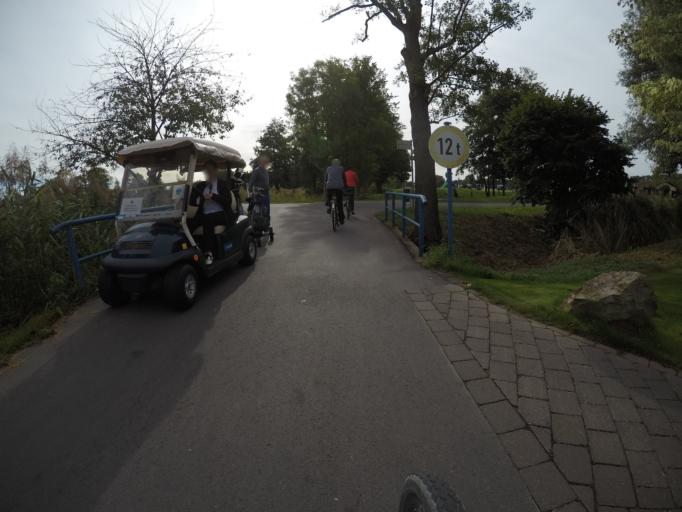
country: DE
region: Baden-Wuerttemberg
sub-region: Karlsruhe Region
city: Kronau
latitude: 49.2447
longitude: 8.6310
